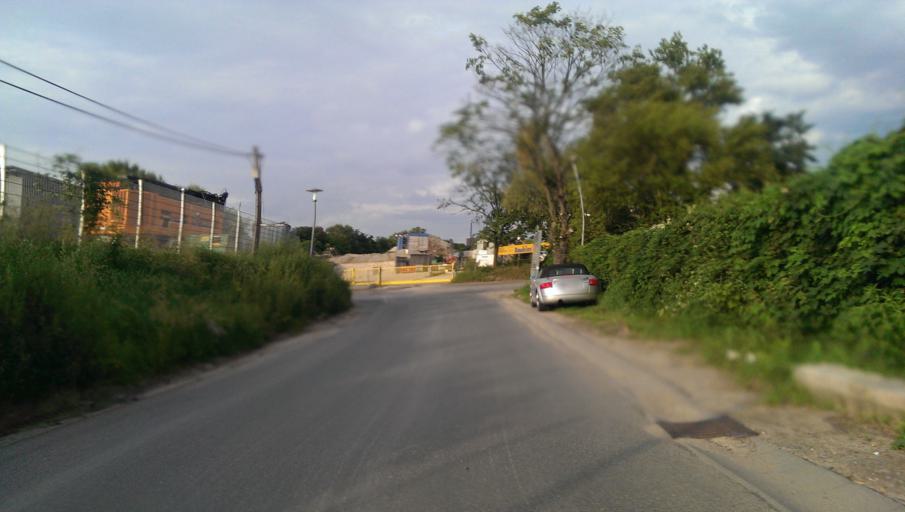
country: DE
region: Brandenburg
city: Teltow
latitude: 52.4125
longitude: 13.2874
